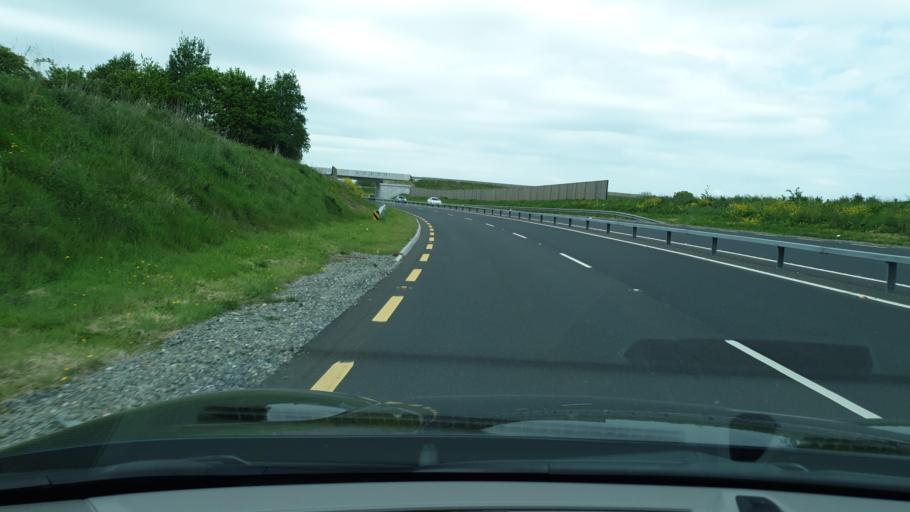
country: IE
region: Leinster
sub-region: Kildare
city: Sallins
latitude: 53.2405
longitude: -6.6765
